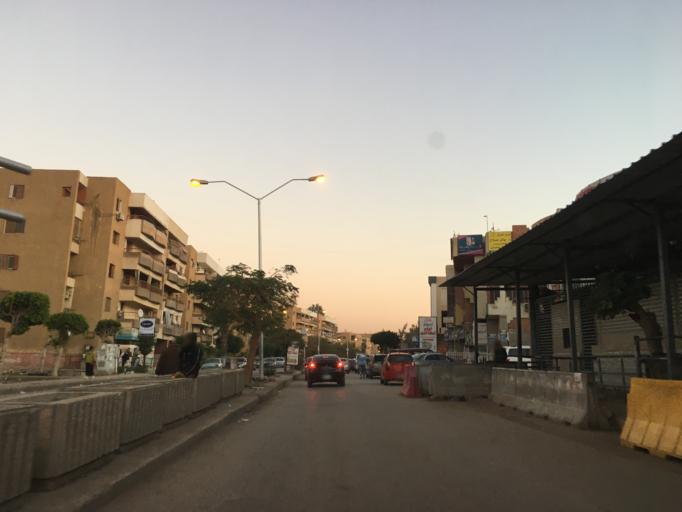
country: EG
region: Al Jizah
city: Madinat Sittah Uktubar
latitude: 29.9833
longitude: 30.9394
